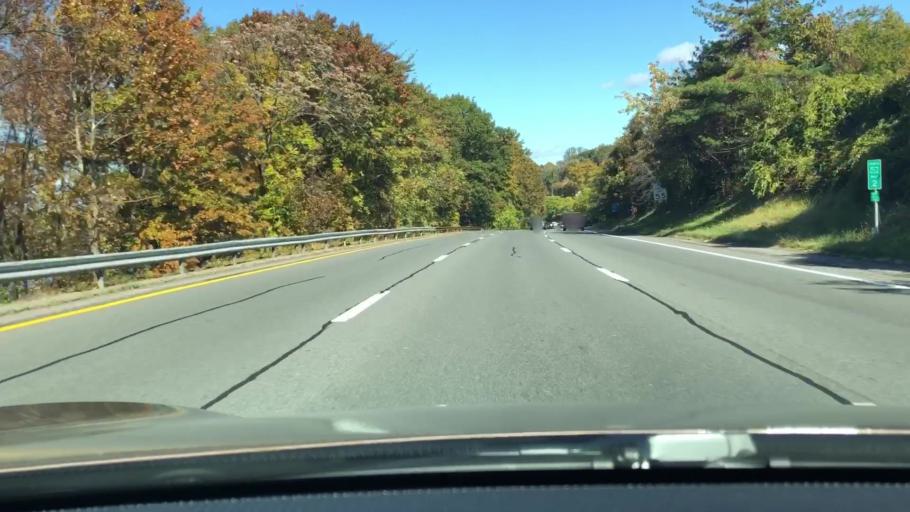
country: US
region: New York
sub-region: Westchester County
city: Tuckahoe
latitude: 40.9614
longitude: -73.8501
